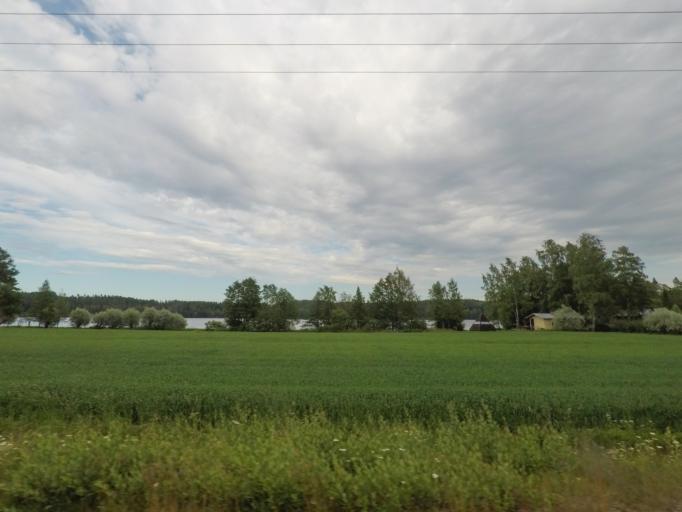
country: FI
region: Uusimaa
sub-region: Porvoo
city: Pukkila
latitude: 60.7580
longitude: 25.4380
